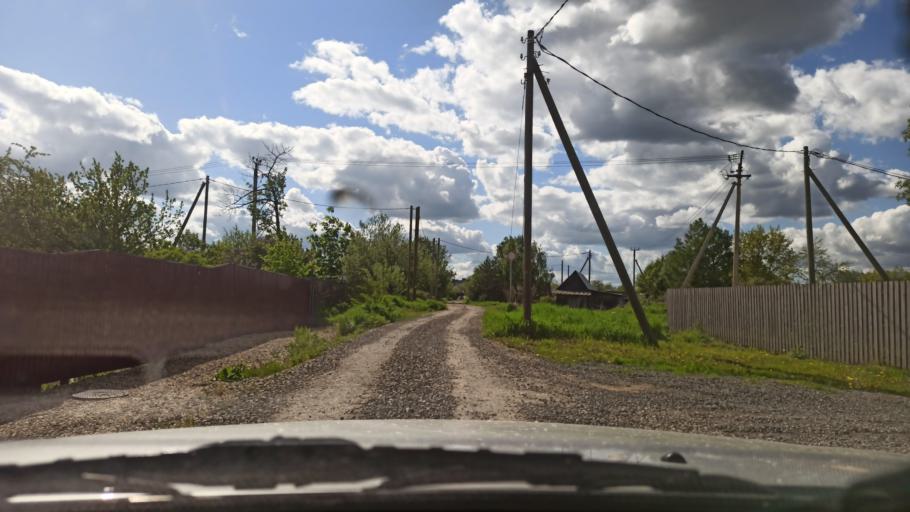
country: RU
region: Vologda
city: Vologda
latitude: 59.3430
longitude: 39.8240
